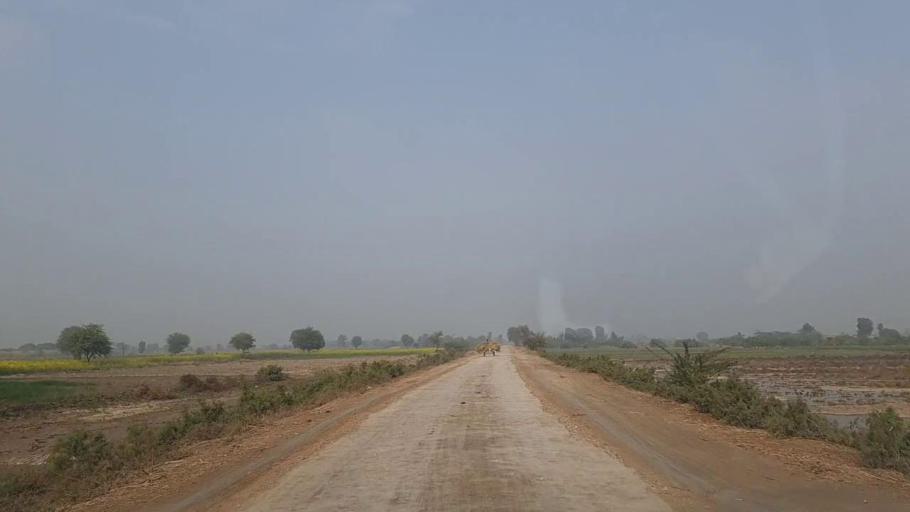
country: PK
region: Sindh
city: Sanghar
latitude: 26.0918
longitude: 68.8980
